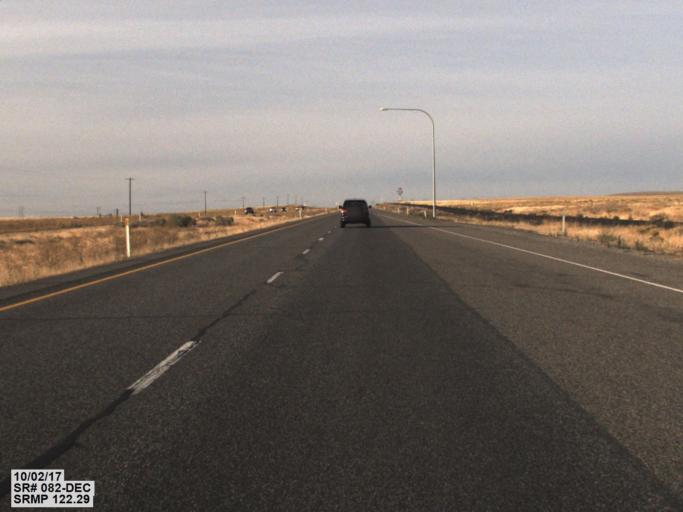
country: US
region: Washington
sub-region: Benton County
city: Highland
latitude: 46.0320
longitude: -119.2245
